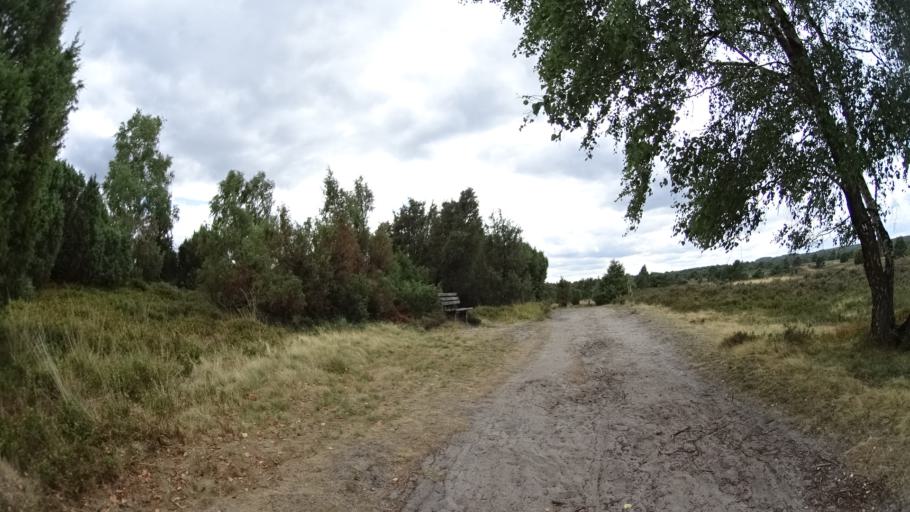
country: DE
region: Lower Saxony
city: Undeloh
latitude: 53.1700
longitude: 9.9876
